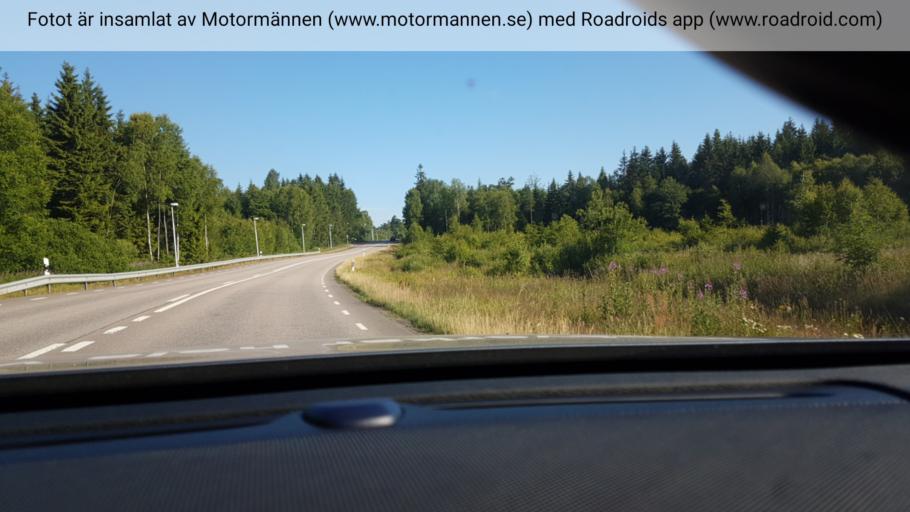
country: SE
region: Skane
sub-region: Hassleholms Kommun
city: Bjarnum
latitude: 56.3148
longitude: 13.6880
